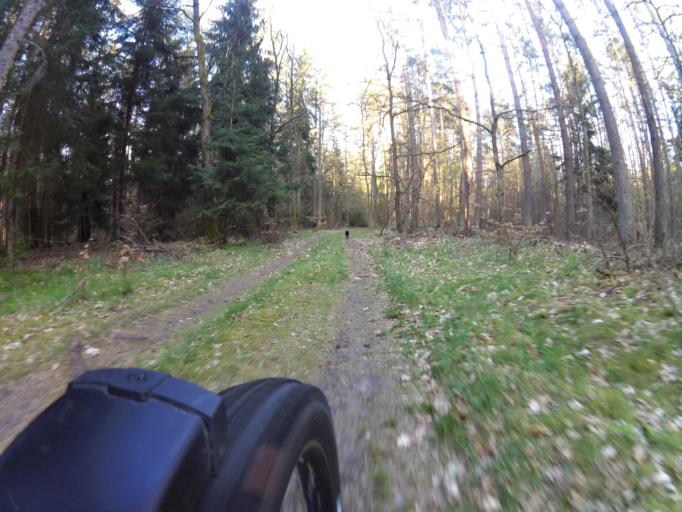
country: PL
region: West Pomeranian Voivodeship
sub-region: Powiat gryficki
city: Ploty
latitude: 53.7521
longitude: 15.3026
